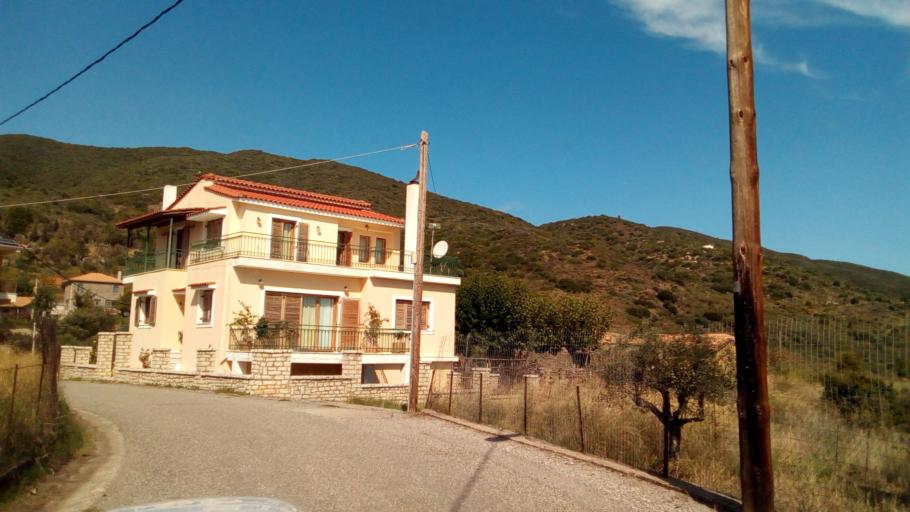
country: GR
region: West Greece
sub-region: Nomos Aitolias kai Akarnanias
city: Antirrio
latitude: 38.3589
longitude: 21.7534
